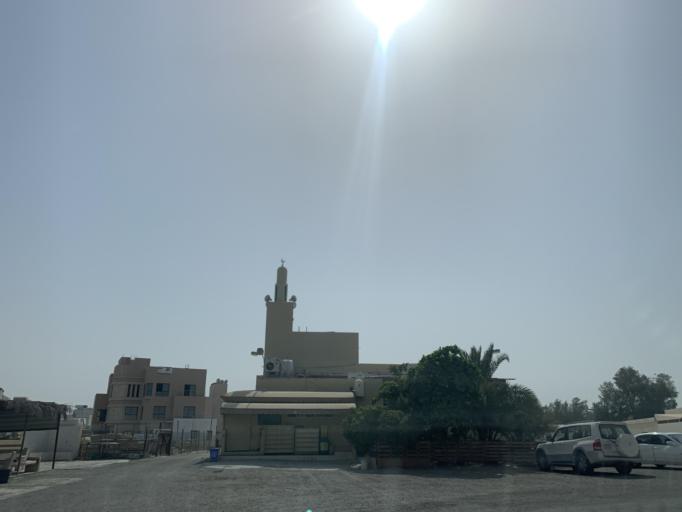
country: BH
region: Manama
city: Jidd Hafs
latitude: 26.2113
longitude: 50.5136
